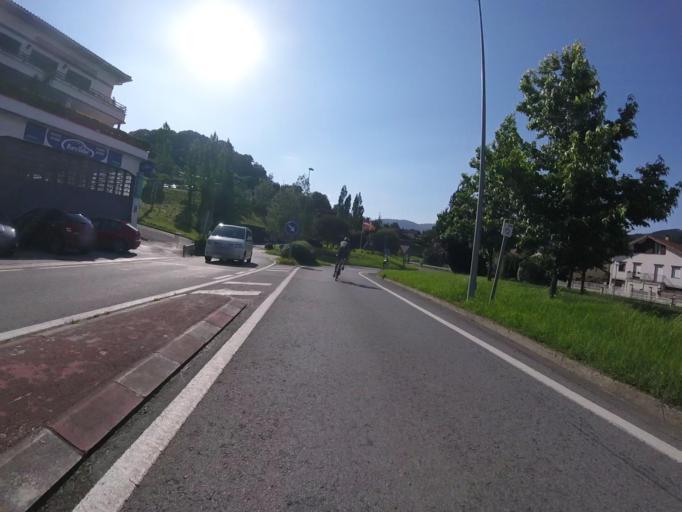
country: ES
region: Basque Country
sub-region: Provincia de Guipuzcoa
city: Asteasu
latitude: 43.1938
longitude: -2.0951
